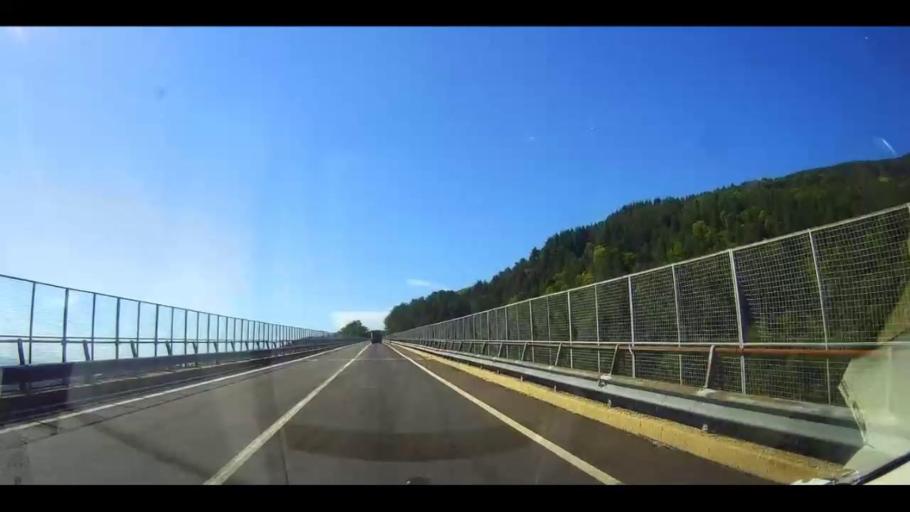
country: IT
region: Calabria
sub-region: Provincia di Cosenza
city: Celico
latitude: 39.3220
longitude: 16.3674
